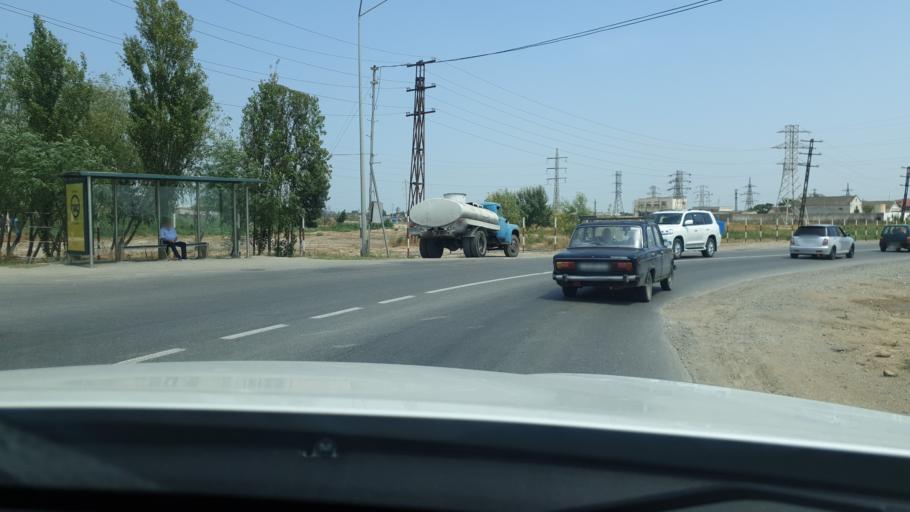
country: AZ
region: Baki
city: Qaracuxur
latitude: 40.3952
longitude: 49.9937
